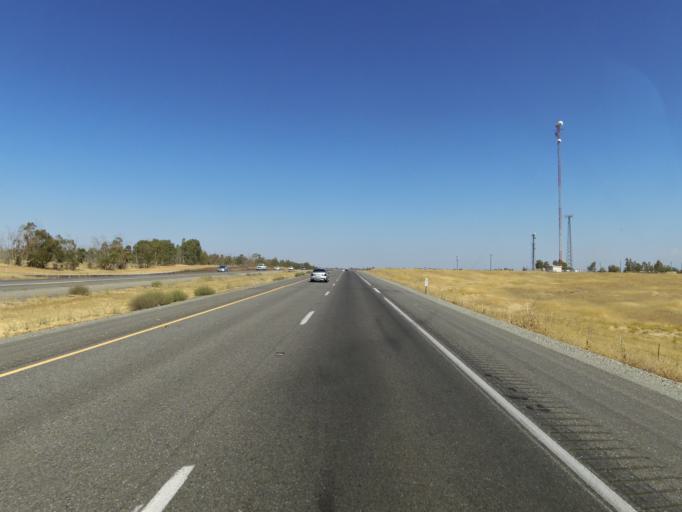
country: US
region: California
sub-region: Tehama County
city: Corning
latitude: 39.8413
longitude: -122.1998
